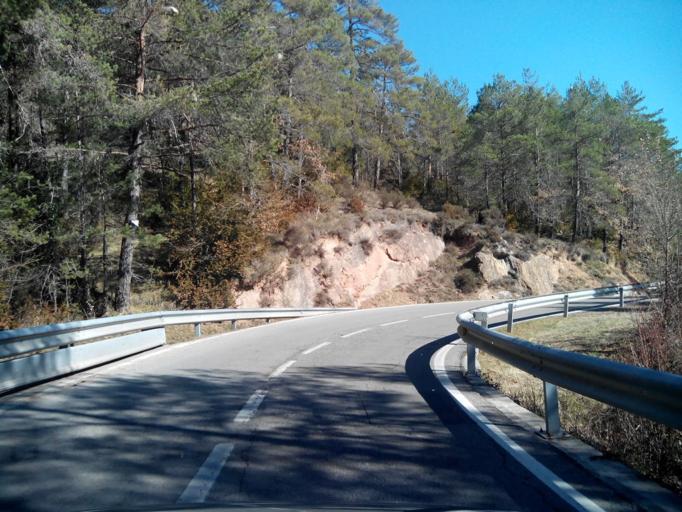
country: ES
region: Catalonia
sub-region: Provincia de Barcelona
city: Vilada
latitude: 42.1309
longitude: 1.9412
